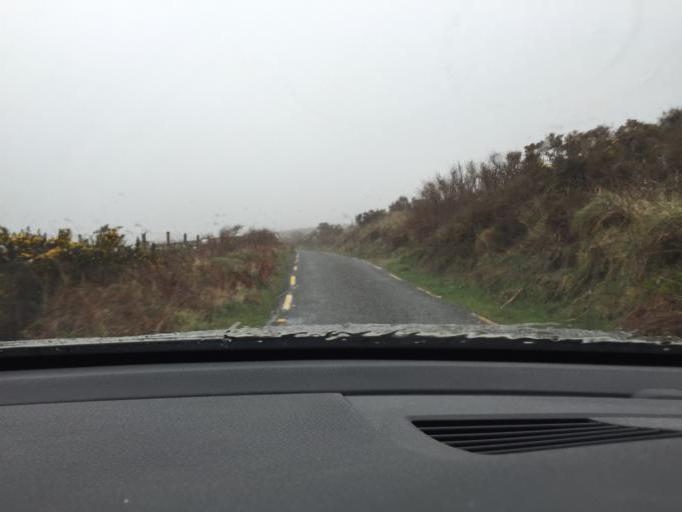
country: IE
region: Munster
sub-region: Ciarrai
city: Dingle
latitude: 52.1341
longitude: -10.4449
